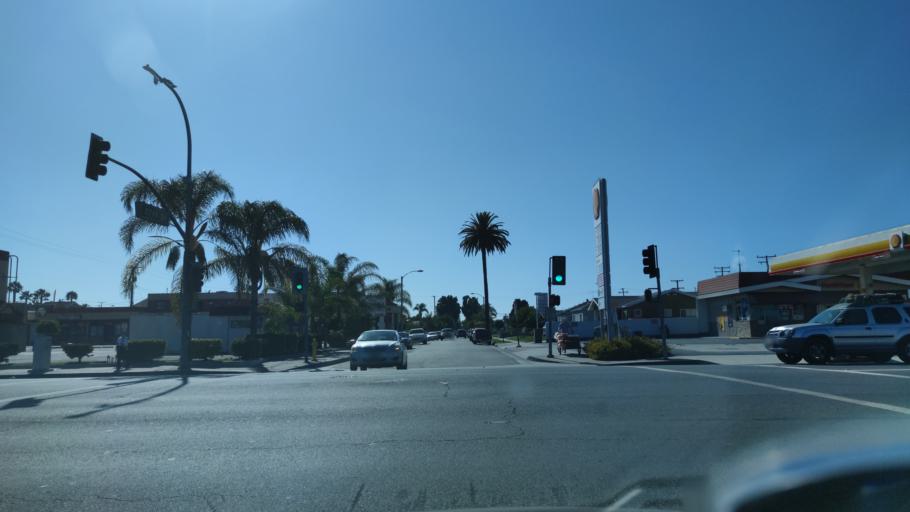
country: US
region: California
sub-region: Los Angeles County
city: Maywood
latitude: 33.9891
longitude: -118.1852
